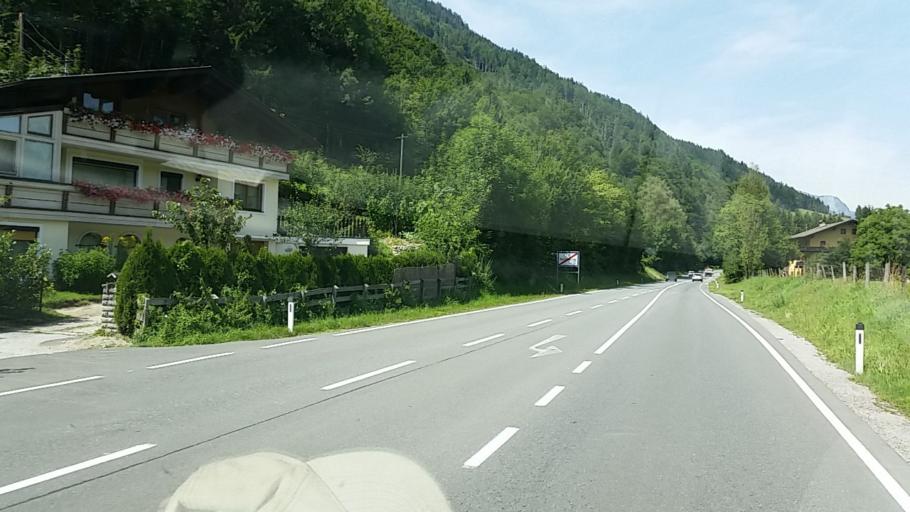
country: AT
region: Salzburg
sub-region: Politischer Bezirk Sankt Johann im Pongau
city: Bischofshofen
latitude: 47.4304
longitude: 13.2126
